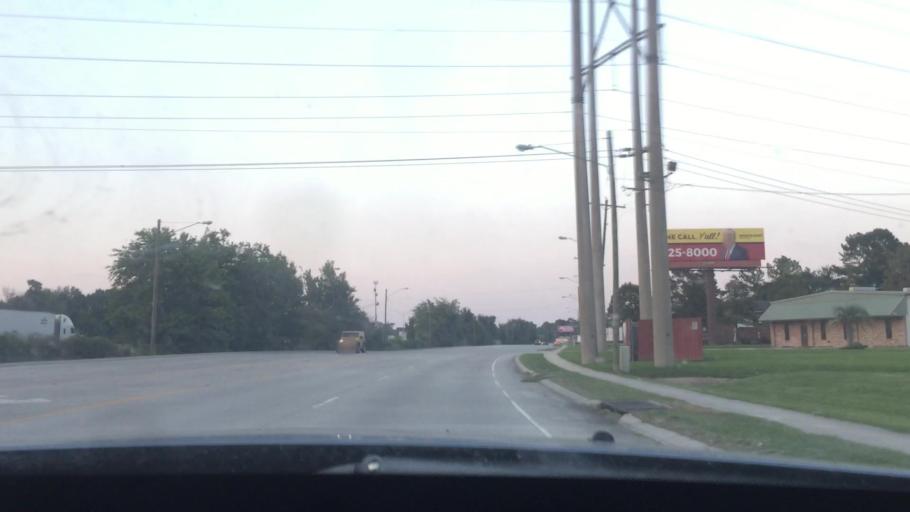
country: US
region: Louisiana
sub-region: East Baton Rouge Parish
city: Westminster
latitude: 30.4304
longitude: -91.0533
